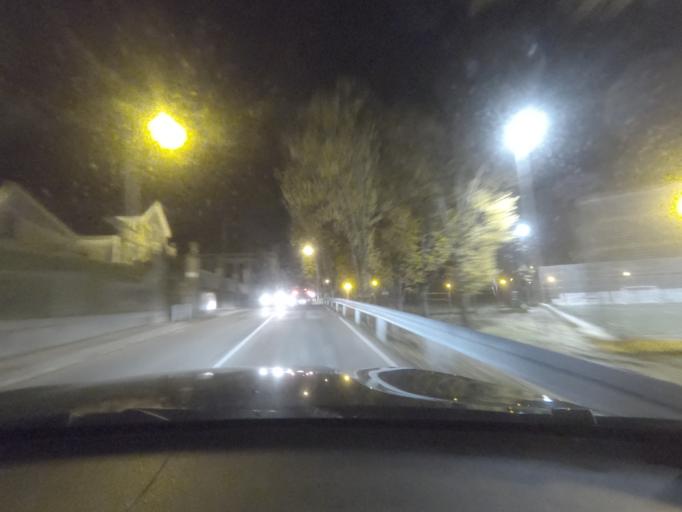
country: PT
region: Vila Real
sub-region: Vila Real
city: Vila Real
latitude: 41.2953
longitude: -7.7389
